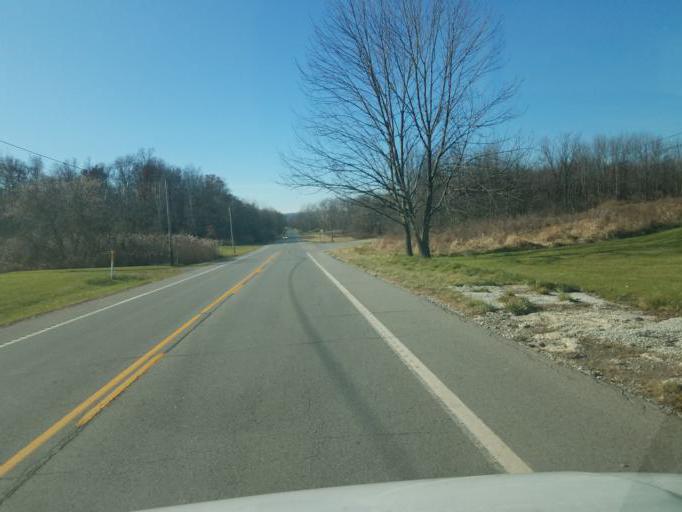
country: US
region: Ohio
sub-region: Richland County
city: Lincoln Heights
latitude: 40.8182
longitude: -82.4021
